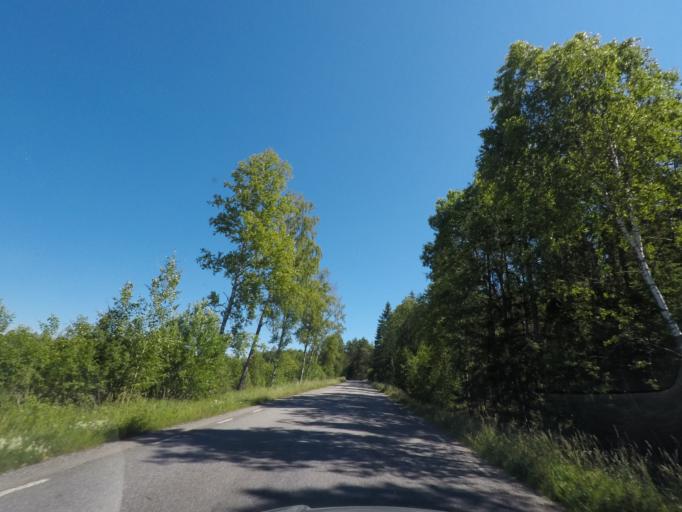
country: SE
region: Uppsala
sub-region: Enkopings Kommun
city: Irsta
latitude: 59.6721
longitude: 16.8983
